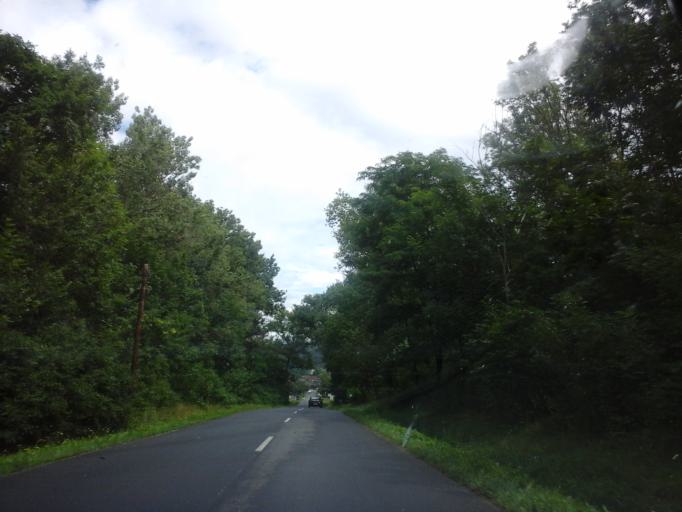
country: HU
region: Borsod-Abauj-Zemplen
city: Rudabanya
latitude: 48.4628
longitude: 20.4957
